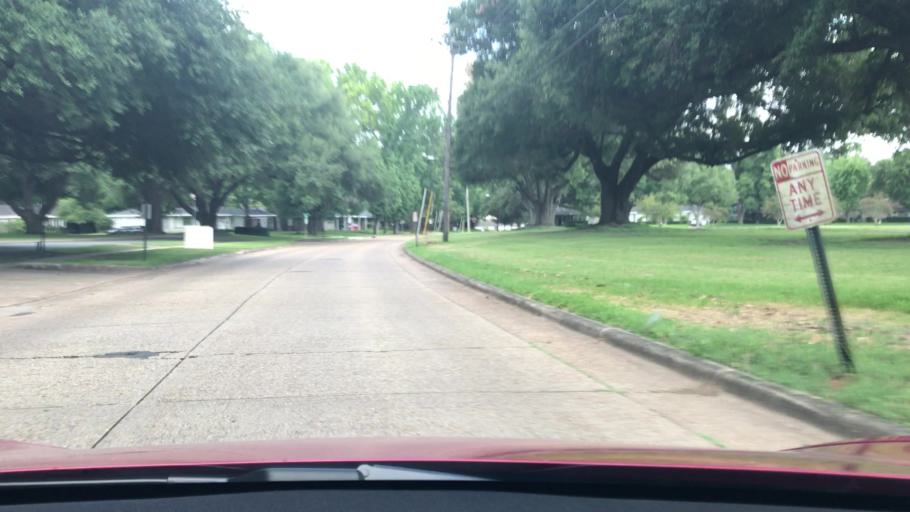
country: US
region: Louisiana
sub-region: Bossier Parish
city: Bossier City
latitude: 32.4600
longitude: -93.7161
